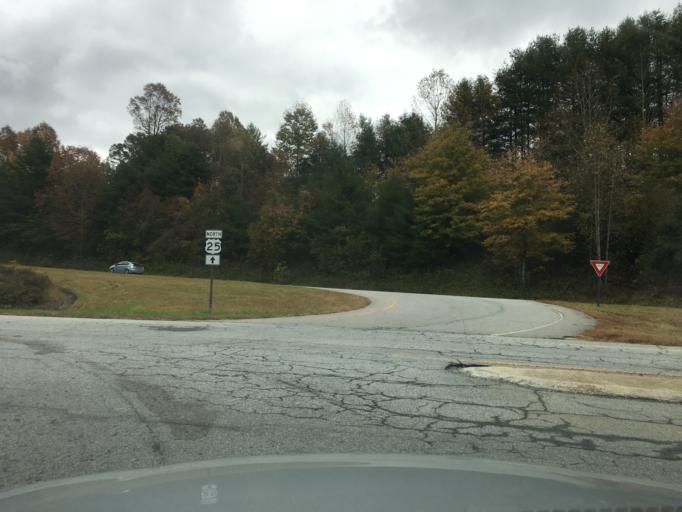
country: US
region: North Carolina
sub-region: Henderson County
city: Flat Rock
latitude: 35.2354
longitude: -82.4167
